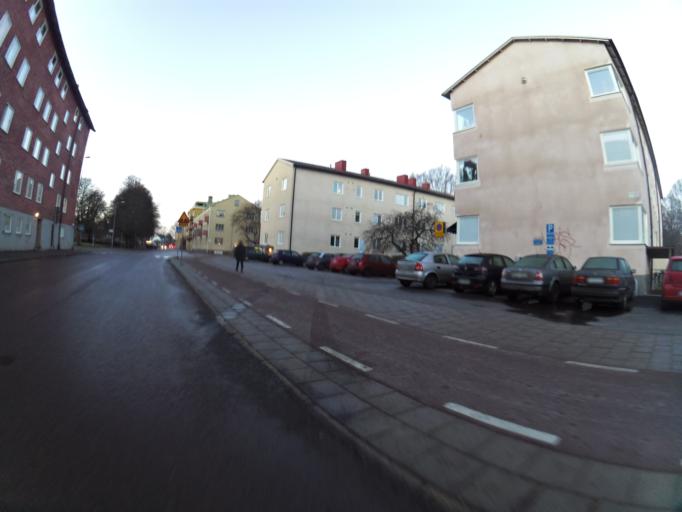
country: SE
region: Gaevleborg
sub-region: Gavle Kommun
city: Gavle
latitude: 60.6692
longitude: 17.1443
